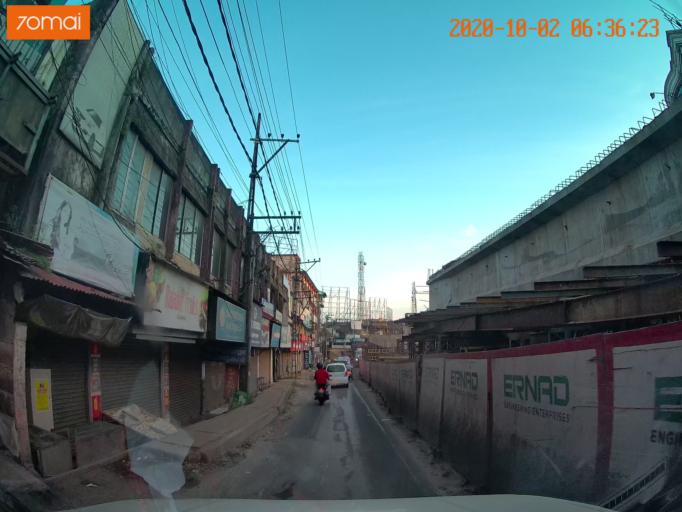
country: IN
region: Kerala
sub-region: Malappuram
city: Ponnani
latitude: 10.7829
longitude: 76.0077
